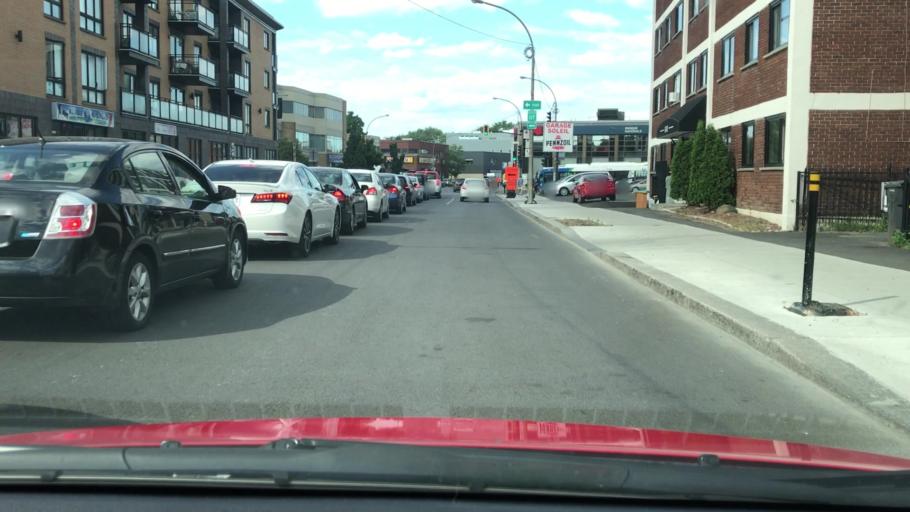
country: CA
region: Quebec
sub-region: Laval
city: Laval
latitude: 45.5305
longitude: -73.7223
